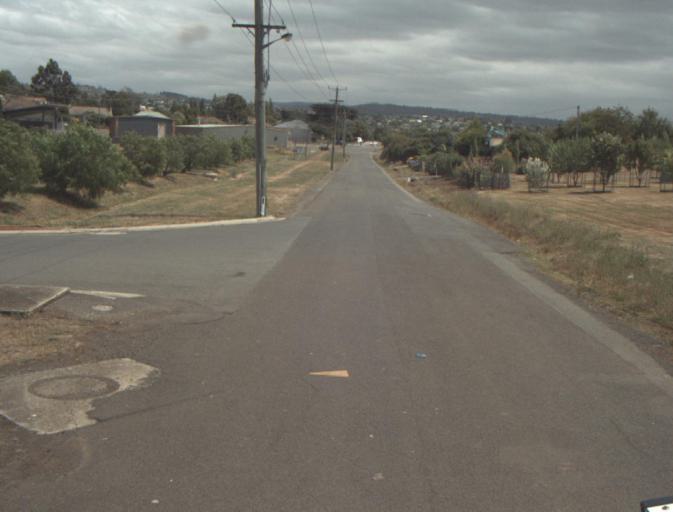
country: AU
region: Tasmania
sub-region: Launceston
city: Newstead
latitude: -41.4352
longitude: 147.1791
